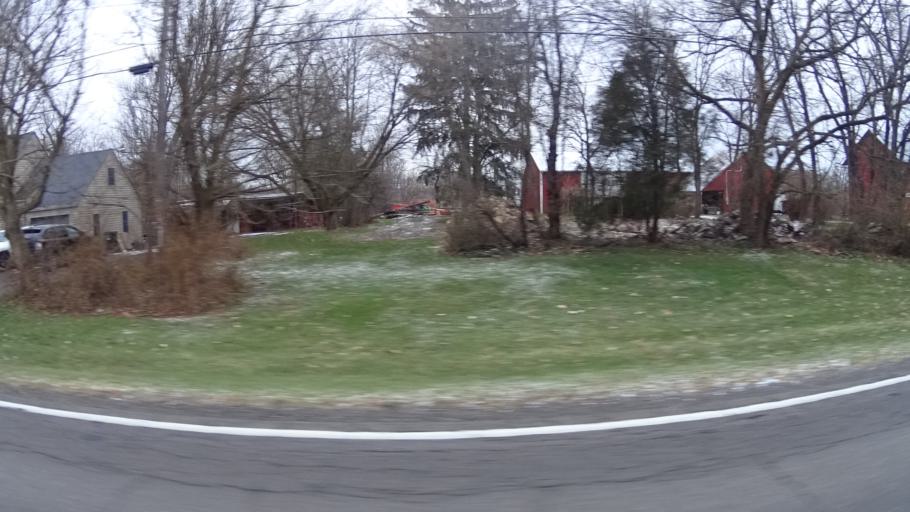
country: US
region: Ohio
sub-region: Lorain County
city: Grafton
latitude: 41.2936
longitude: -82.0510
